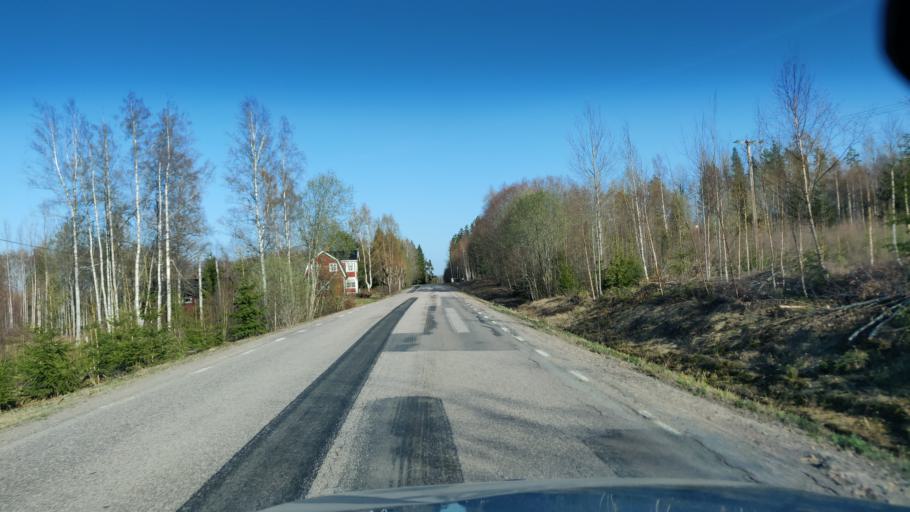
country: SE
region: Vaermland
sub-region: Munkfors Kommun
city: Munkfors
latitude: 59.9706
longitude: 13.4546
